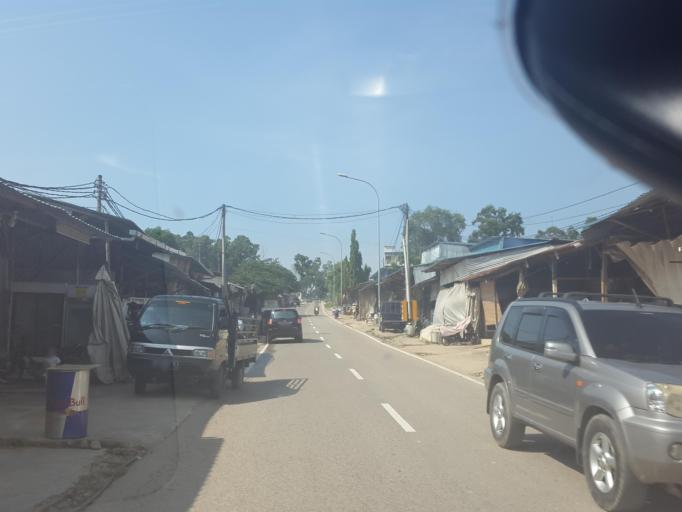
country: SG
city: Singapore
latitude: 1.1740
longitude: 104.0116
